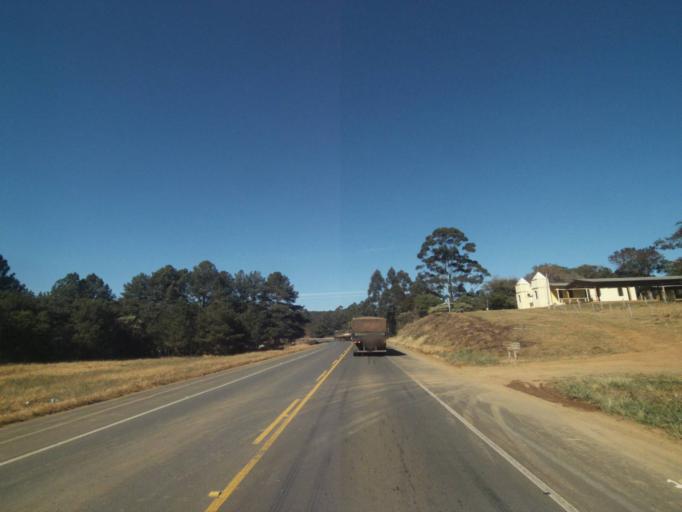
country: BR
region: Parana
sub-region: Tibagi
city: Tibagi
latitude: -24.5765
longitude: -50.4504
